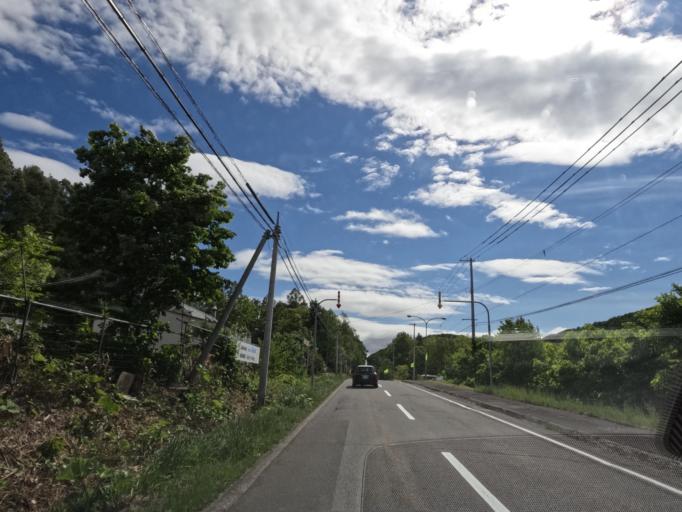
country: JP
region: Hokkaido
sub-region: Asahikawa-shi
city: Asahikawa
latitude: 43.8383
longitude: 142.5417
